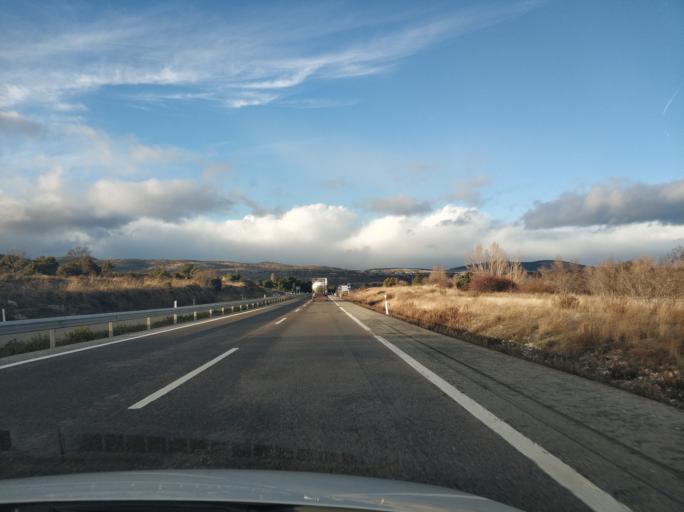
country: ES
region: Madrid
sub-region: Provincia de Madrid
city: La Cabrera
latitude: 40.8987
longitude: -3.6059
